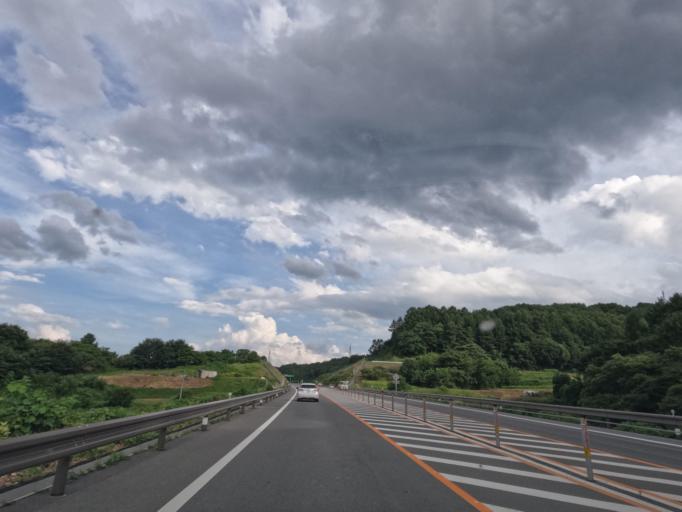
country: JP
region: Nagano
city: Saku
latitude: 36.2054
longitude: 138.4571
